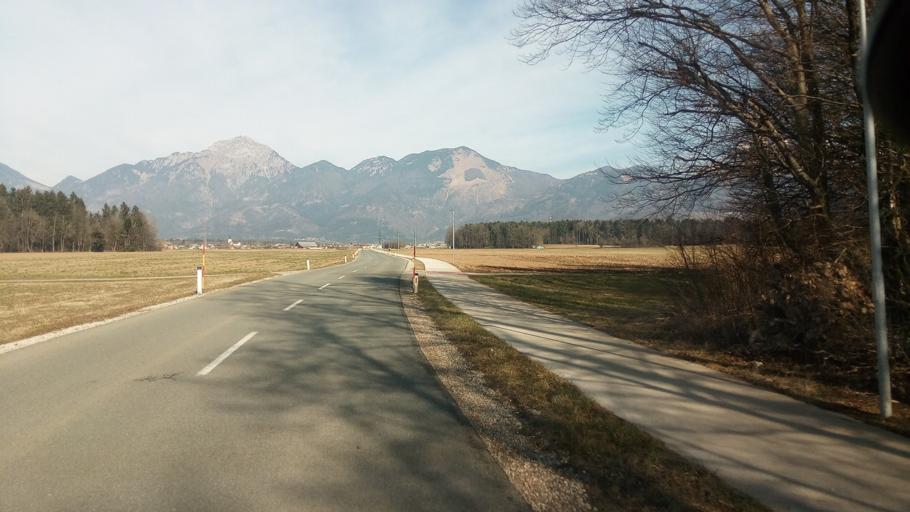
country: SI
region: Sencur
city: Sencur
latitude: 46.2583
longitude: 14.4182
